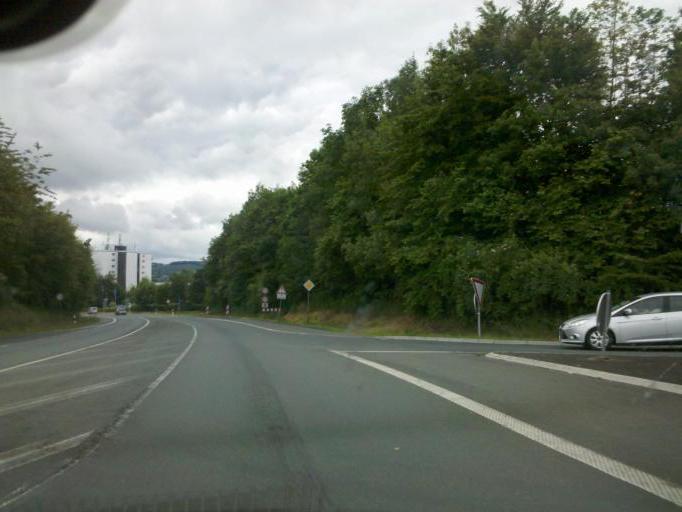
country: DE
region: North Rhine-Westphalia
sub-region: Regierungsbezirk Arnsberg
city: Meschede
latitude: 51.3643
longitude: 8.2898
